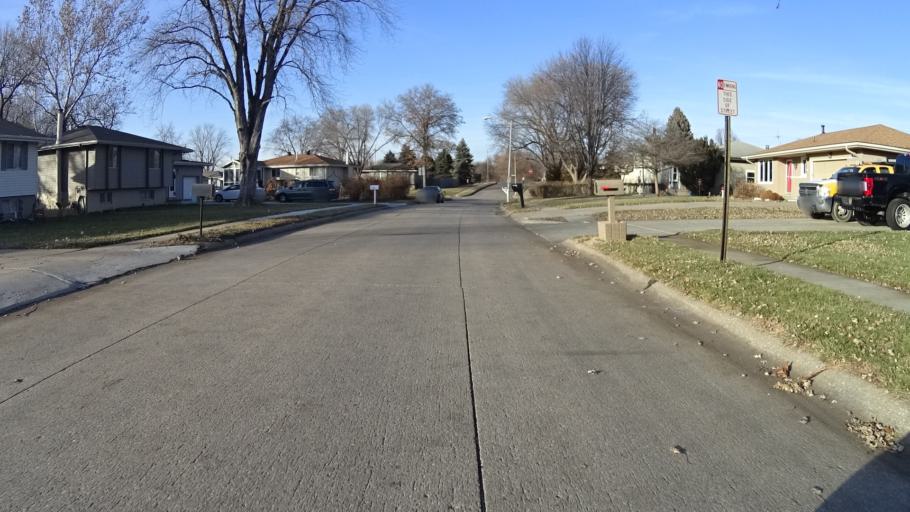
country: US
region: Nebraska
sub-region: Sarpy County
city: La Vista
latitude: 41.1894
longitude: -95.9996
